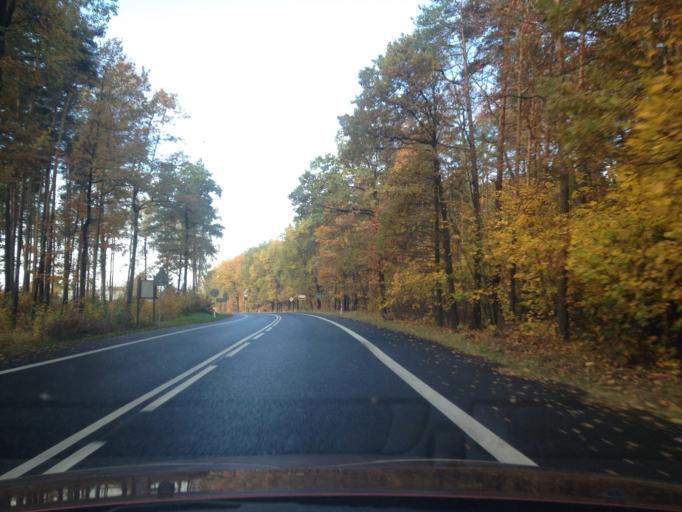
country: PL
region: Lower Silesian Voivodeship
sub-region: Powiat zgorzelecki
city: Lagow
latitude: 51.1586
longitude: 15.0578
